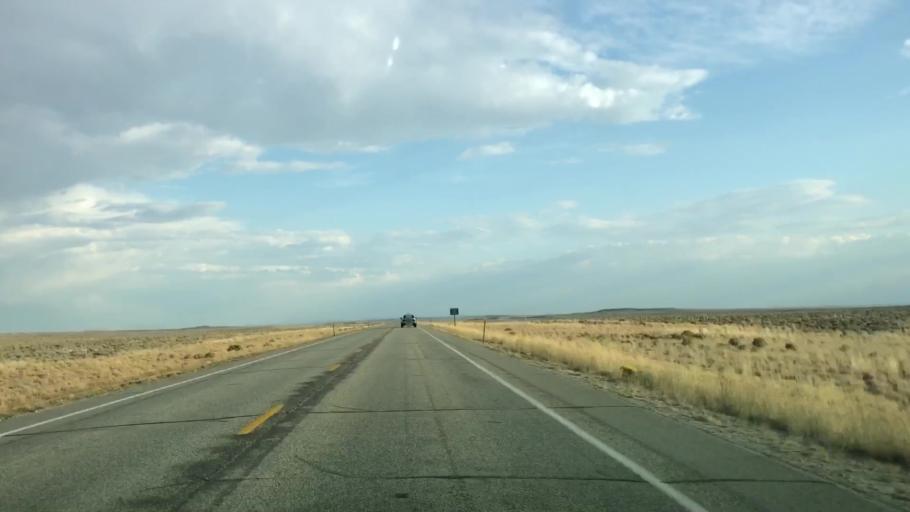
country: US
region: Wyoming
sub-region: Sublette County
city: Pinedale
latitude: 42.3932
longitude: -109.5421
